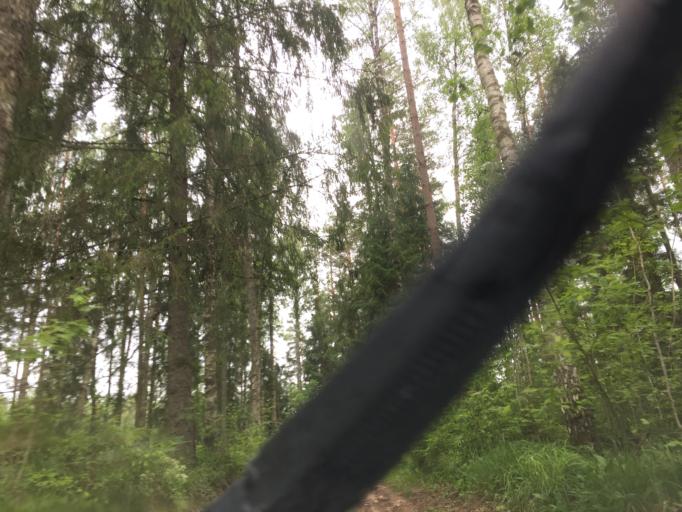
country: LV
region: Tukuma Rajons
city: Tukums
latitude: 57.0310
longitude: 23.0758
